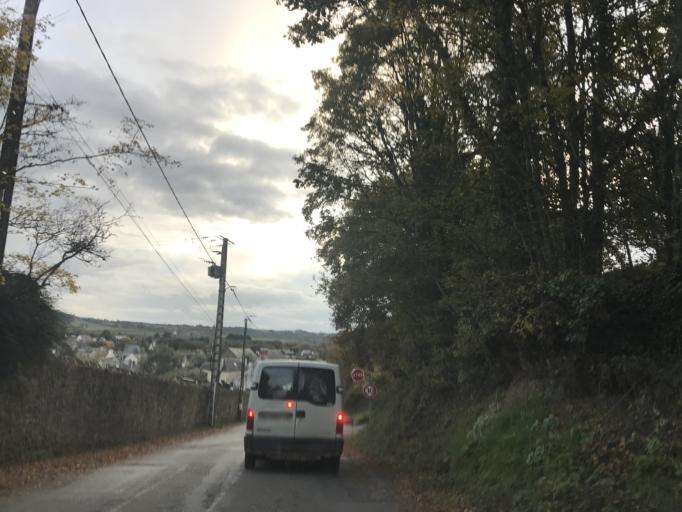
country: FR
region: Brittany
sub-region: Departement du Finistere
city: Le Faou
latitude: 48.2990
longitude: -4.1785
